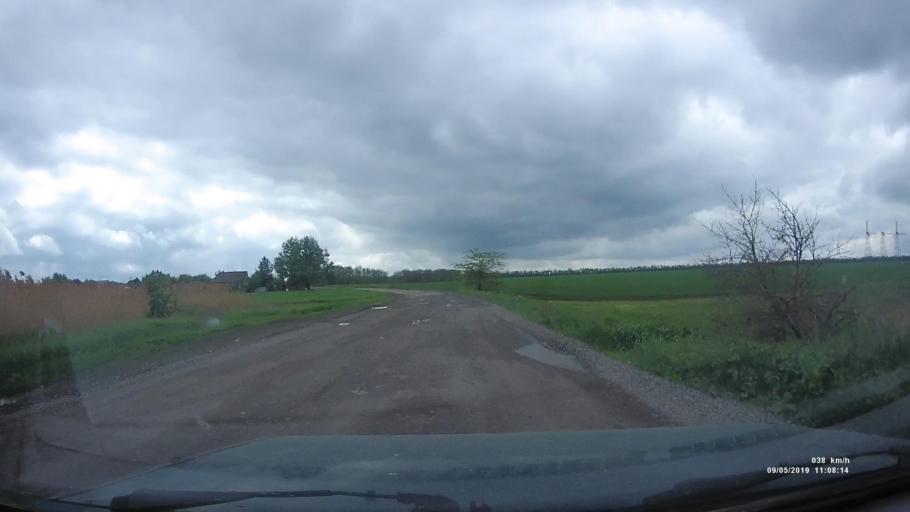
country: RU
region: Krasnodarskiy
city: Kanelovskaya
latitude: 46.7904
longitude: 39.2092
